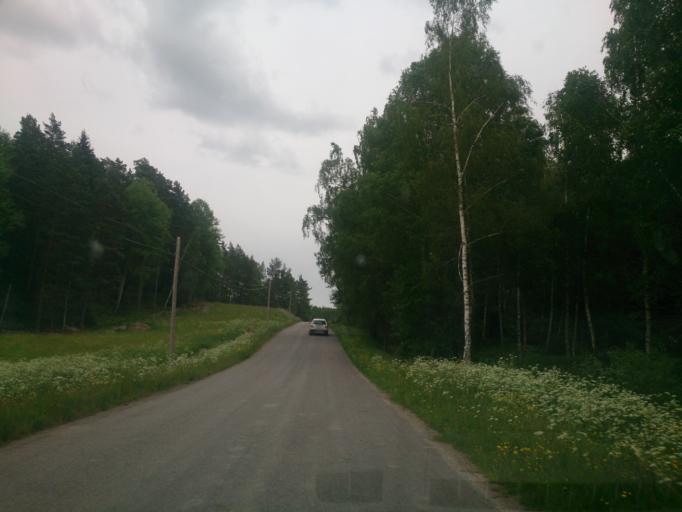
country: SE
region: OEstergoetland
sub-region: Valdemarsviks Kommun
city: Gusum
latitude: 58.3122
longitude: 16.3496
